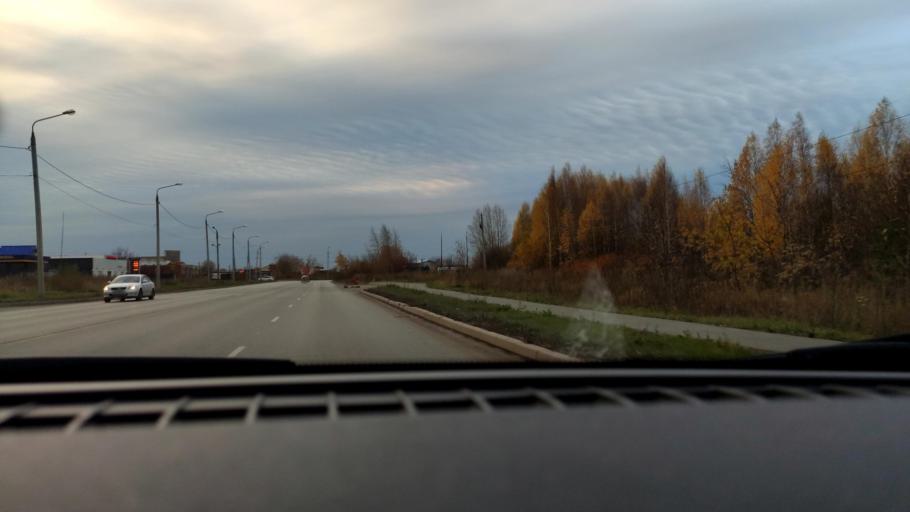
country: RU
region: Perm
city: Kondratovo
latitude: 57.9577
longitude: 56.1845
